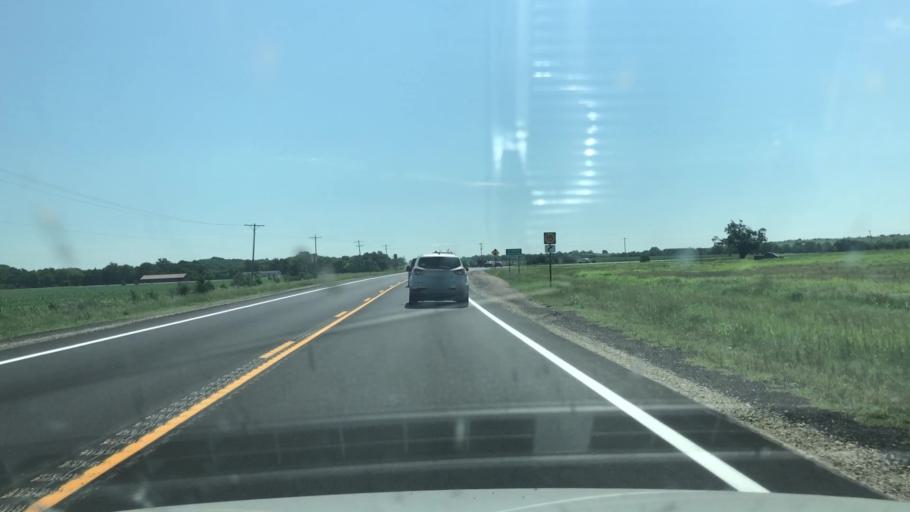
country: US
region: Kansas
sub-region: Butler County
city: Douglass
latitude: 37.3901
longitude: -97.0098
